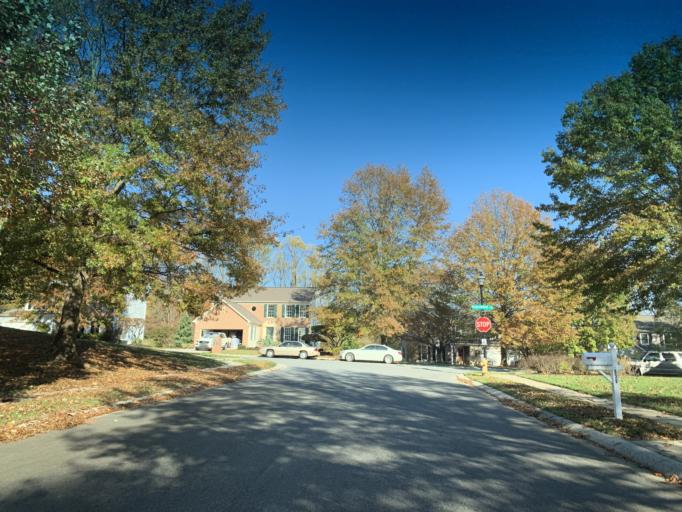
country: US
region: Maryland
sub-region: Harford County
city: Bel Air South
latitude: 39.5088
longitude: -76.3121
